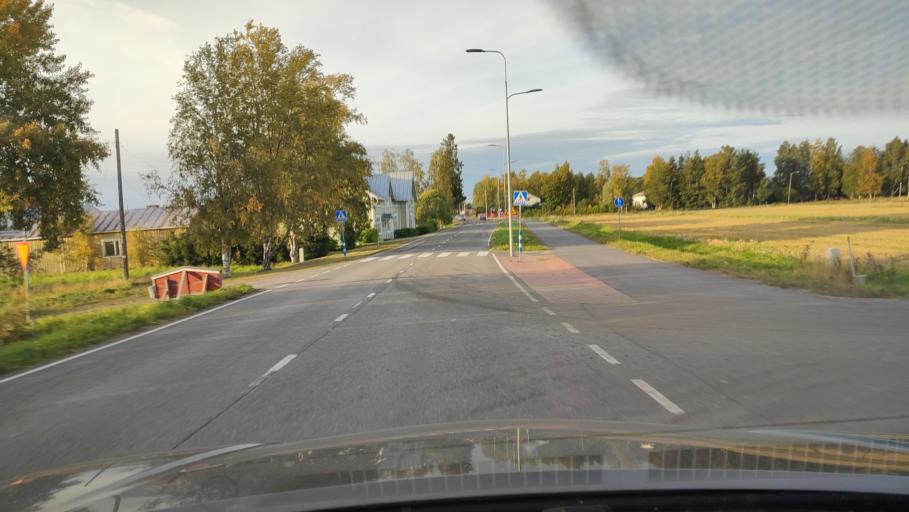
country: FI
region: Ostrobothnia
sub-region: Sydosterbotten
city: Kristinestad
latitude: 62.2487
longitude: 21.5211
